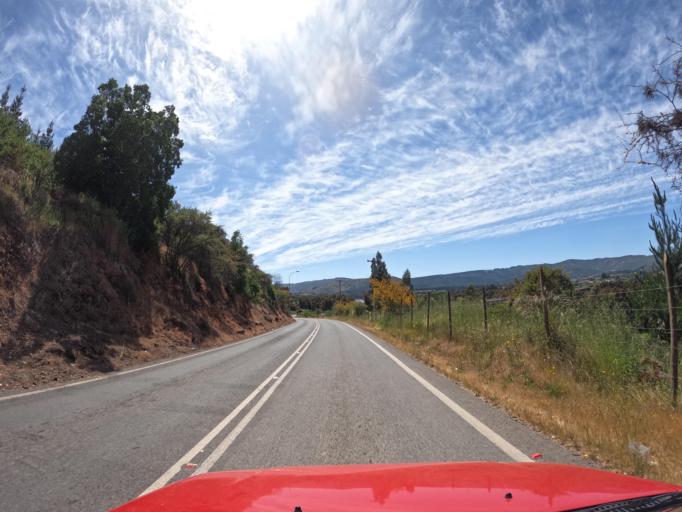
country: CL
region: Maule
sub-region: Provincia de Talca
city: Talca
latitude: -34.9908
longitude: -71.8106
